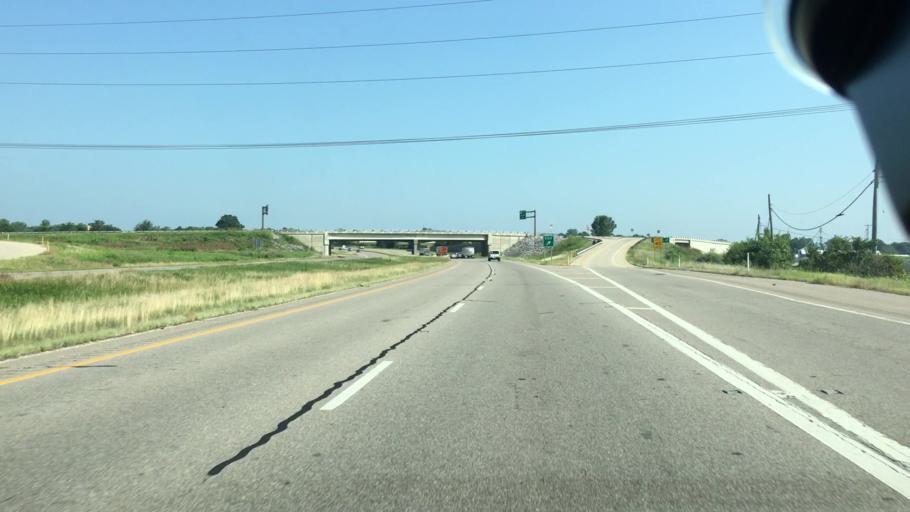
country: US
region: Indiana
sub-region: Gibson County
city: Princeton
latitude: 38.3102
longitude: -87.5676
